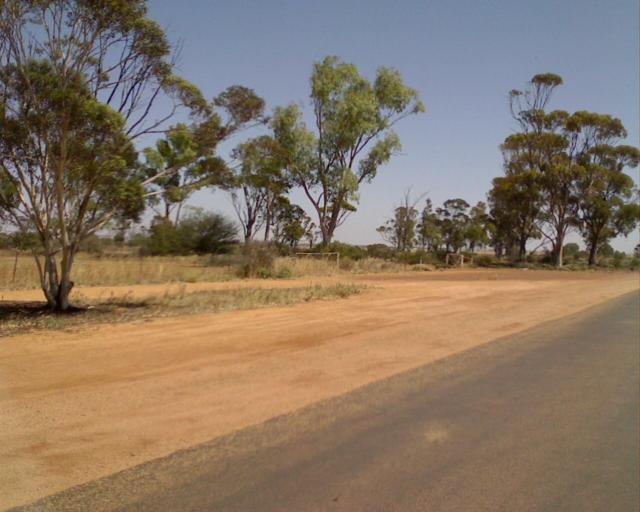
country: AU
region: Western Australia
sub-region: Merredin
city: Merredin
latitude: -30.9114
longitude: 118.2095
